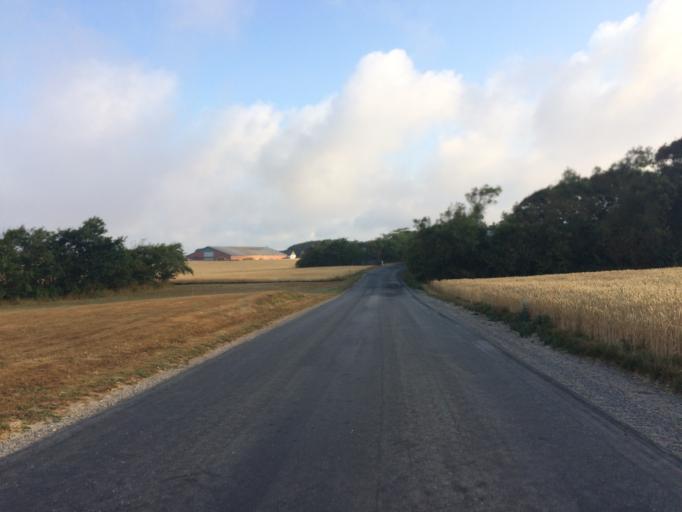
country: DK
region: Central Jutland
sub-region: Holstebro Kommune
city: Vinderup
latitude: 56.5857
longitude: 8.7560
